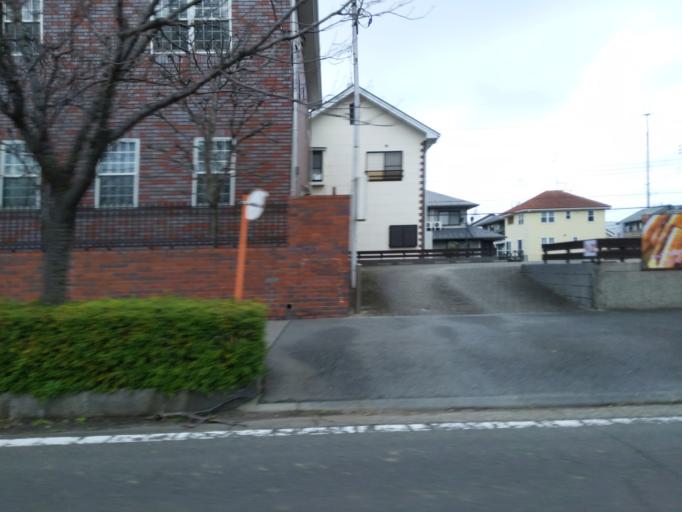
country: JP
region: Ibaraki
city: Ryugasaki
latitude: 35.9300
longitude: 140.2015
